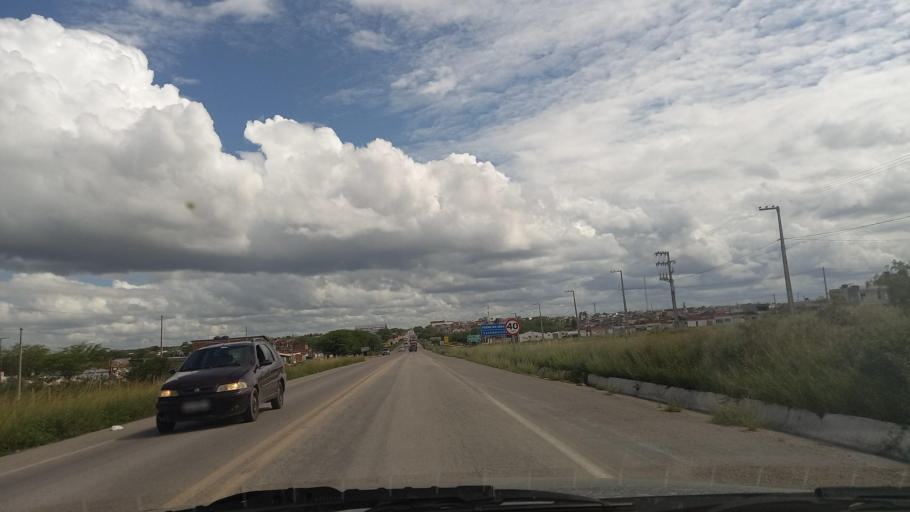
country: BR
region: Pernambuco
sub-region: Cachoeirinha
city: Cachoeirinha
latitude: -8.4852
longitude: -36.2273
